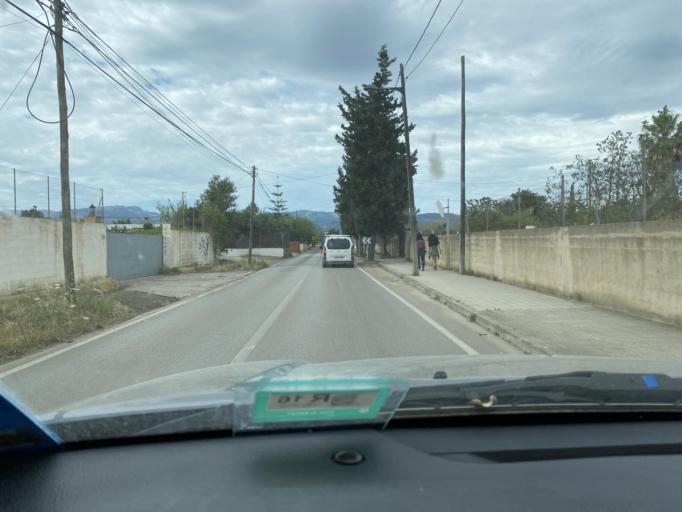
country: ES
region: Balearic Islands
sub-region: Illes Balears
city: Palma
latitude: 39.6108
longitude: 2.6806
